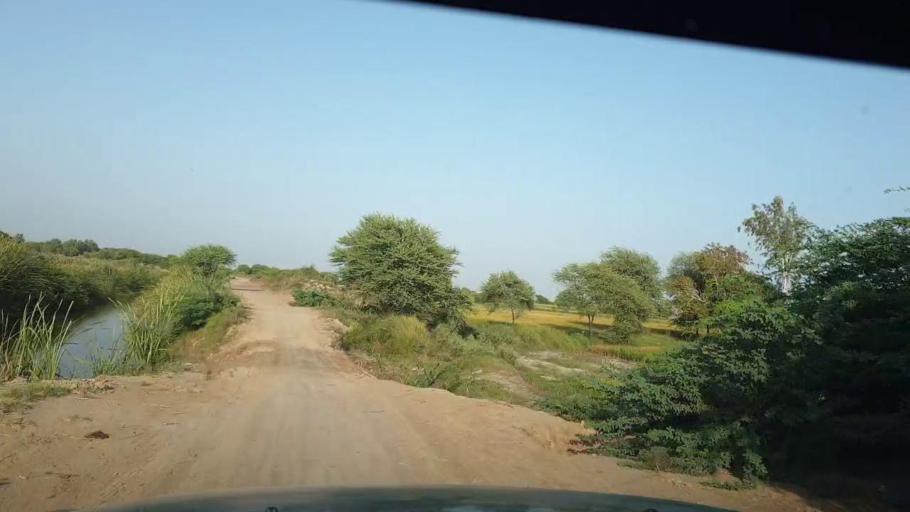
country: PK
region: Sindh
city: Rajo Khanani
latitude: 25.0275
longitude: 68.7722
